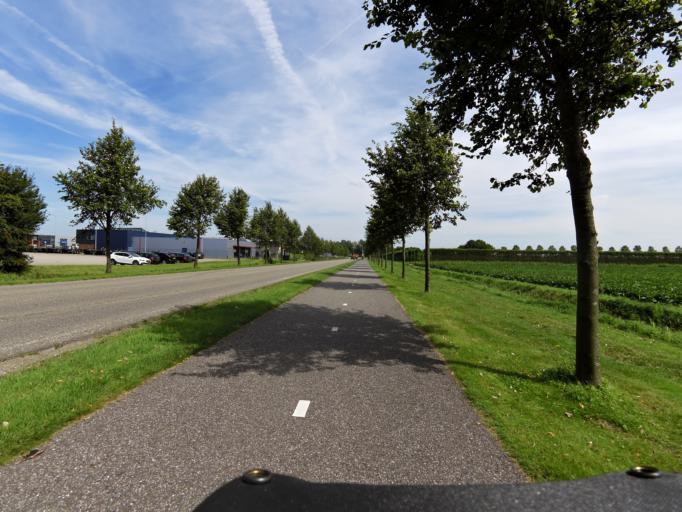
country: NL
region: South Holland
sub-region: Gemeente Goeree-Overflakkee
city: Dirksland
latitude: 51.7488
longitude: 4.1161
